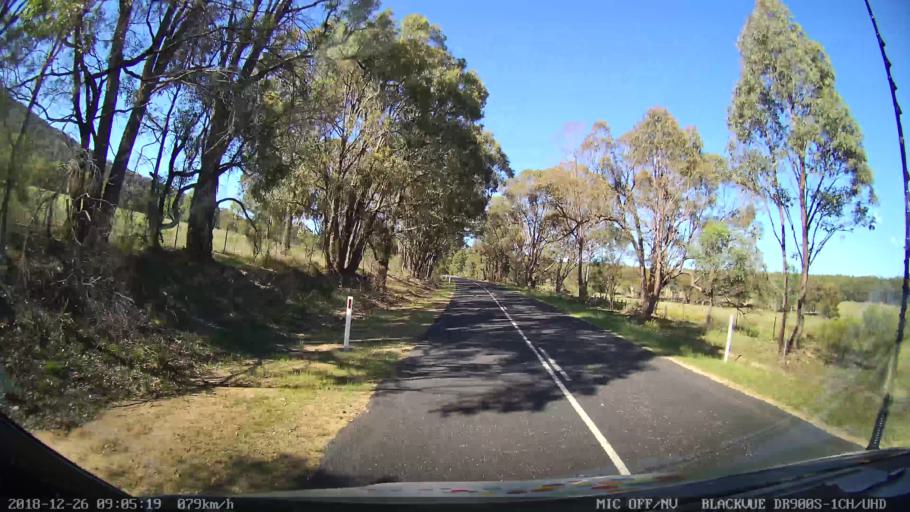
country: AU
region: New South Wales
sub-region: Mid-Western Regional
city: Kandos
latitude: -32.6816
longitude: 150.0087
